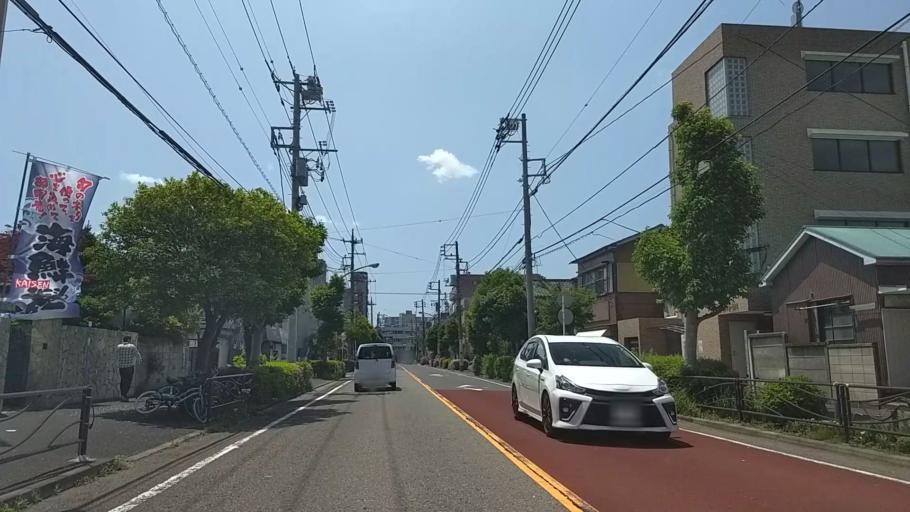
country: JP
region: Kanagawa
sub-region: Kawasaki-shi
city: Kawasaki
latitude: 35.5203
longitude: 139.7194
